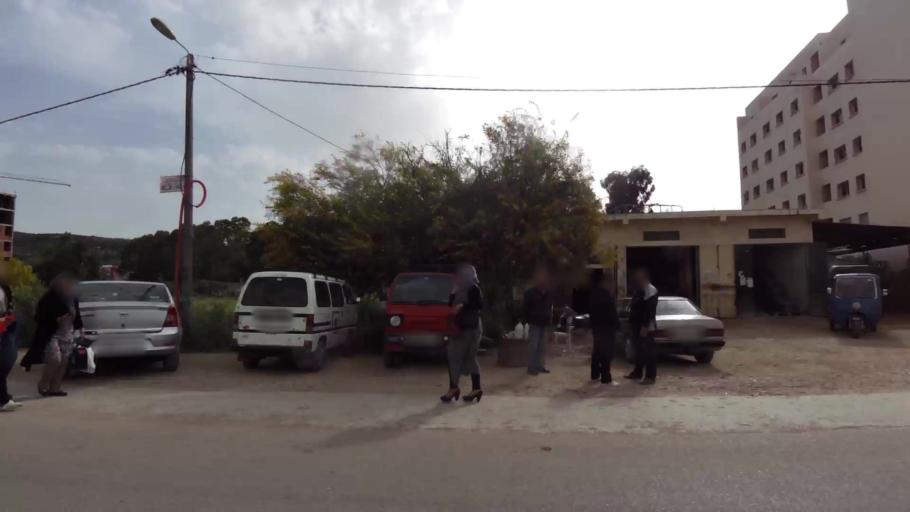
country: MA
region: Tanger-Tetouan
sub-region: Tanger-Assilah
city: Boukhalef
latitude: 35.7066
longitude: -5.9055
